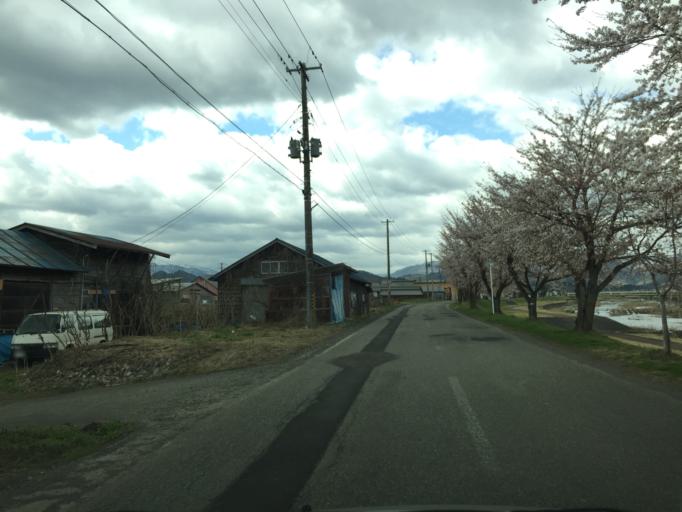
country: JP
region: Fukushima
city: Kitakata
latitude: 37.4491
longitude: 139.8377
